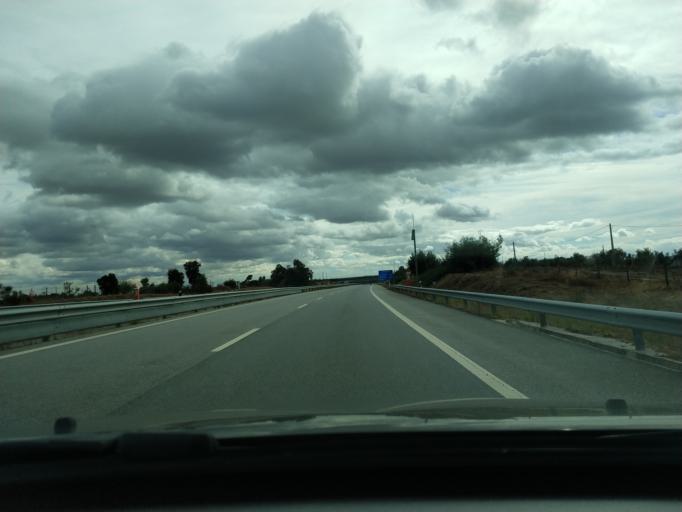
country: PT
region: Guarda
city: Alcains
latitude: 40.0211
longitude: -7.4659
